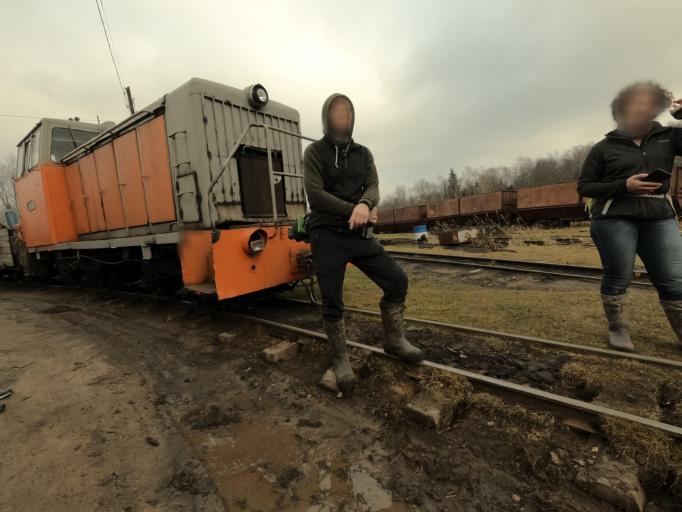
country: RU
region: Leningrad
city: Nurma
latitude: 59.5985
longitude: 31.2022
